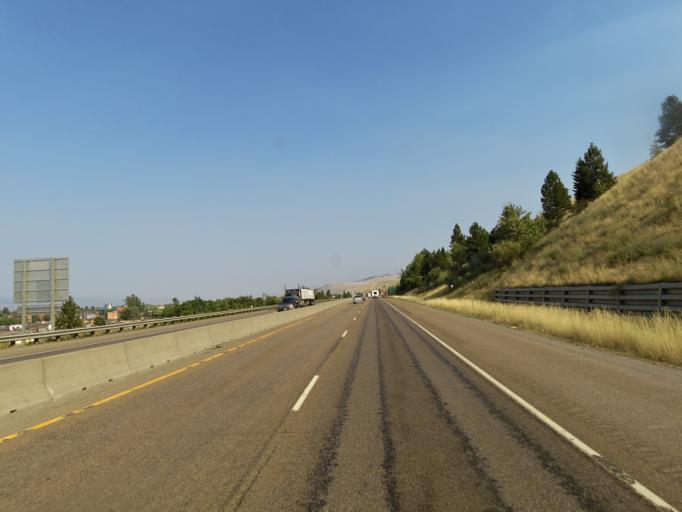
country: US
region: Montana
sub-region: Missoula County
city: Missoula
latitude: 46.8751
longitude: -113.9868
